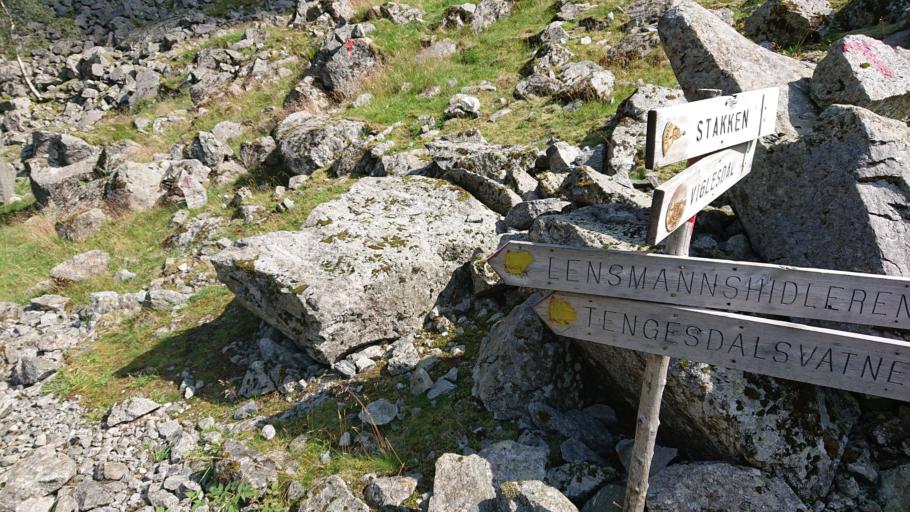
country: NO
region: Rogaland
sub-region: Hjelmeland
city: Hjelmelandsvagen
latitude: 59.1979
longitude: 6.4498
